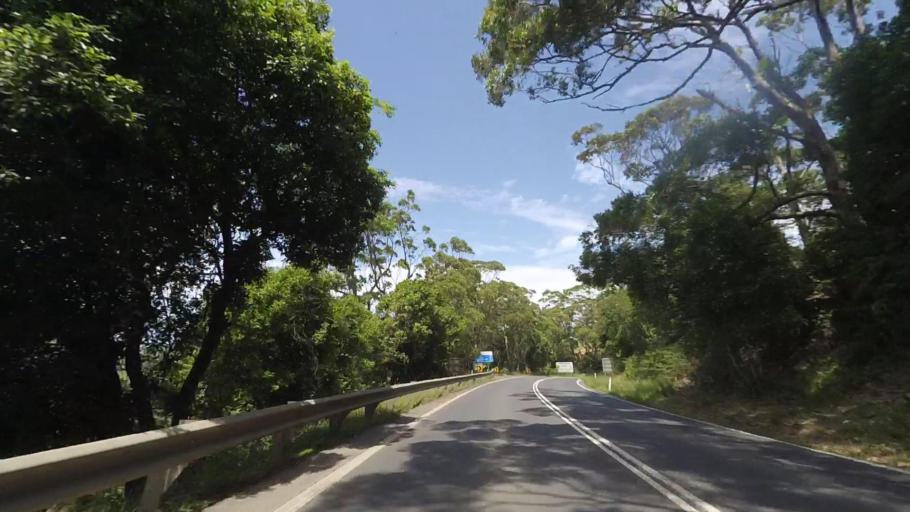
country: AU
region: New South Wales
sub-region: Shoalhaven Shire
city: Berry
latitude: -34.7523
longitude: 150.7500
